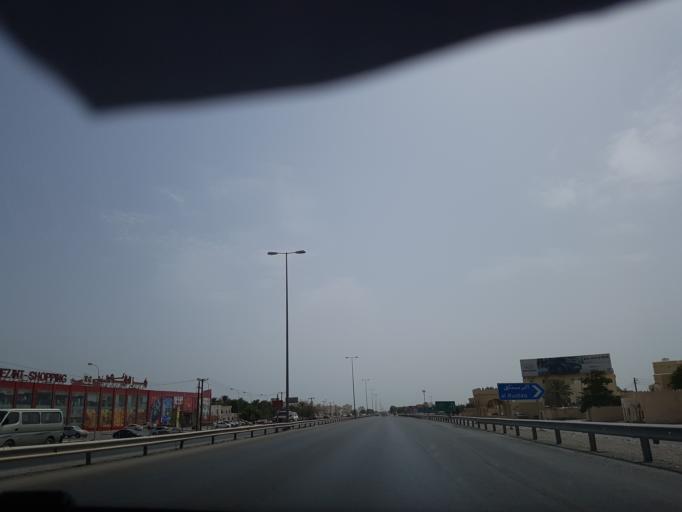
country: OM
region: Al Batinah
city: As Suwayq
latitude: 23.7536
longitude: 57.5705
